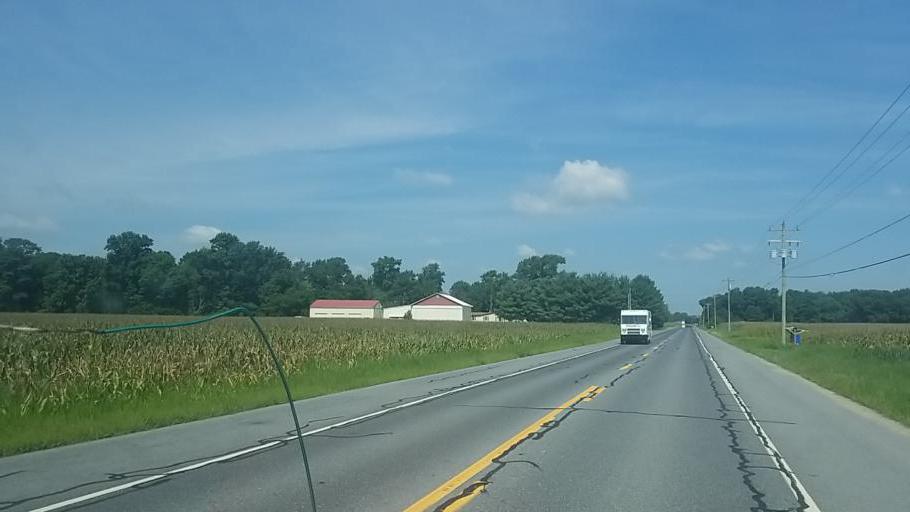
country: US
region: Delaware
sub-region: Sussex County
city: Seaford
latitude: 38.6777
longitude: -75.5800
